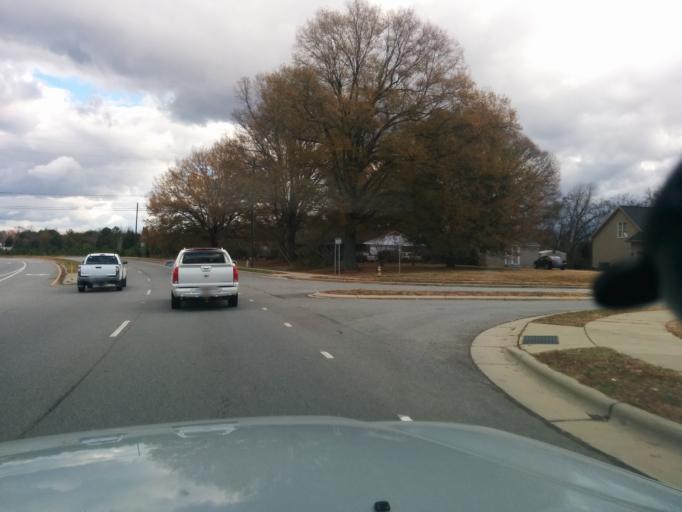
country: US
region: North Carolina
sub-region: Catawba County
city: Lake Norman of Catawba
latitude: 35.5689
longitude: -80.8985
